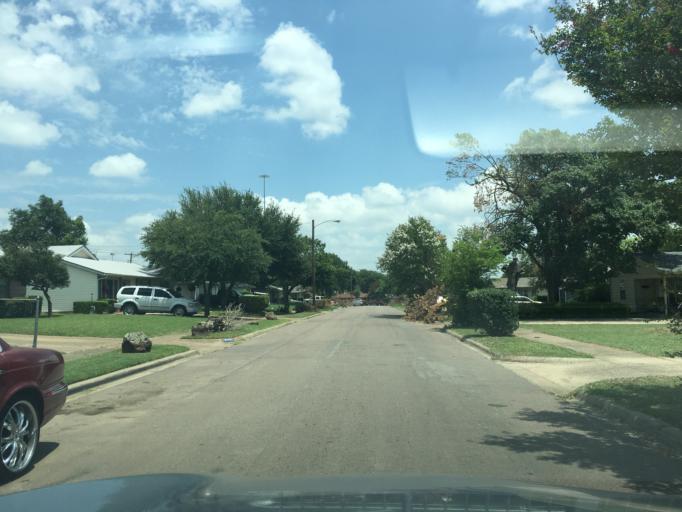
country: US
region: Texas
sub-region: Dallas County
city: Richardson
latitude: 32.9216
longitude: -96.7578
